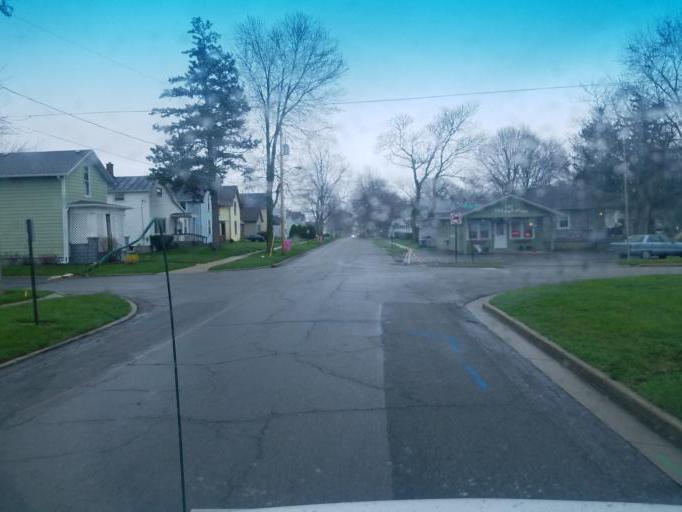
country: US
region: Ohio
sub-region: Hancock County
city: Findlay
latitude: 41.0514
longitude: -83.6600
